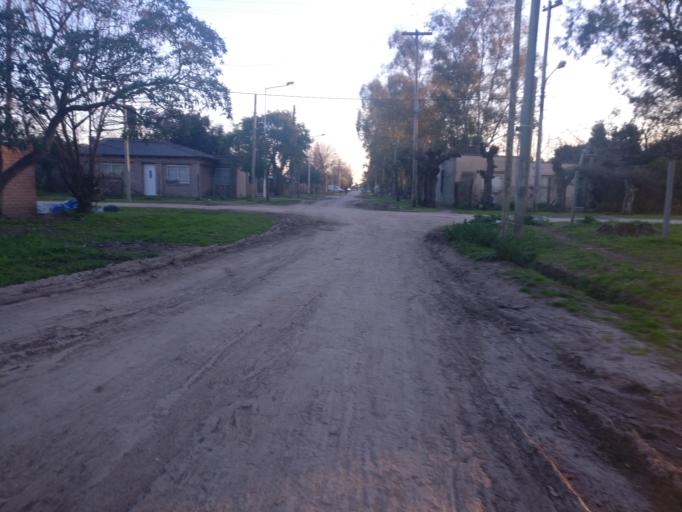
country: AR
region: Buenos Aires
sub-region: Partido de Ezeiza
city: Ezeiza
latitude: -34.9424
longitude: -58.6093
